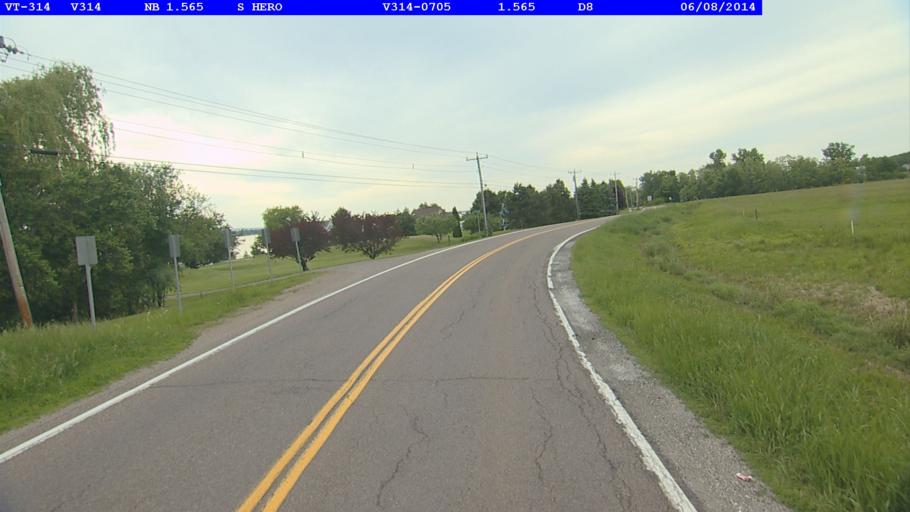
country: US
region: New York
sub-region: Clinton County
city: Cumberland Head
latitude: 44.6771
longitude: -73.3467
